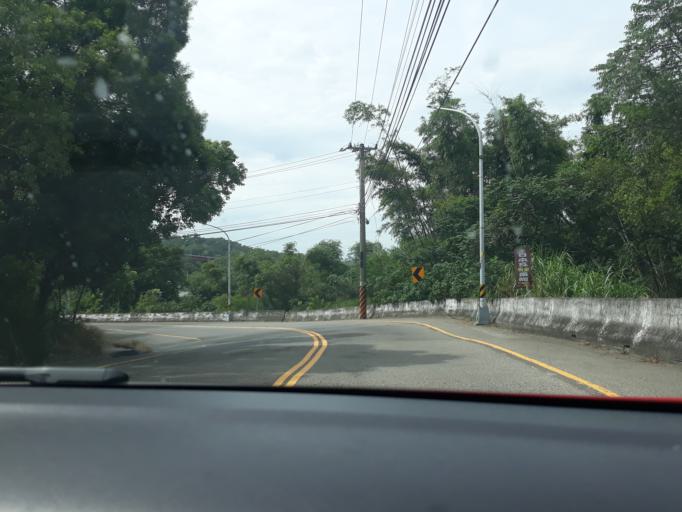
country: TW
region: Taiwan
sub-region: Miaoli
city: Miaoli
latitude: 24.5528
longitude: 120.8048
